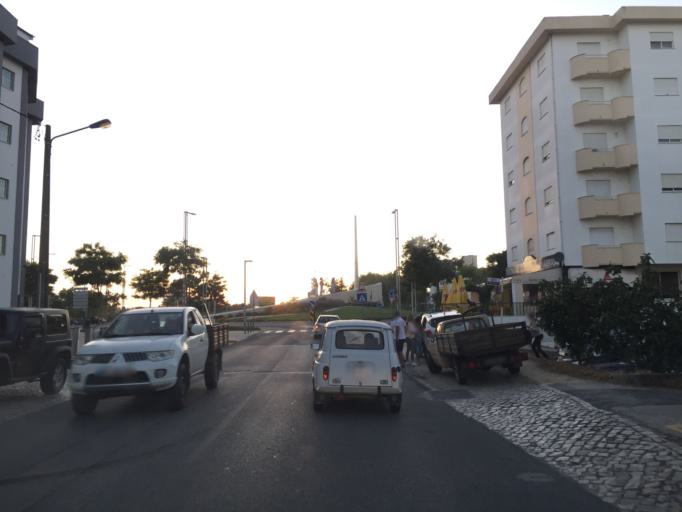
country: PT
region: Santarem
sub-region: Ourem
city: Fatima
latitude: 39.6251
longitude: -8.6648
